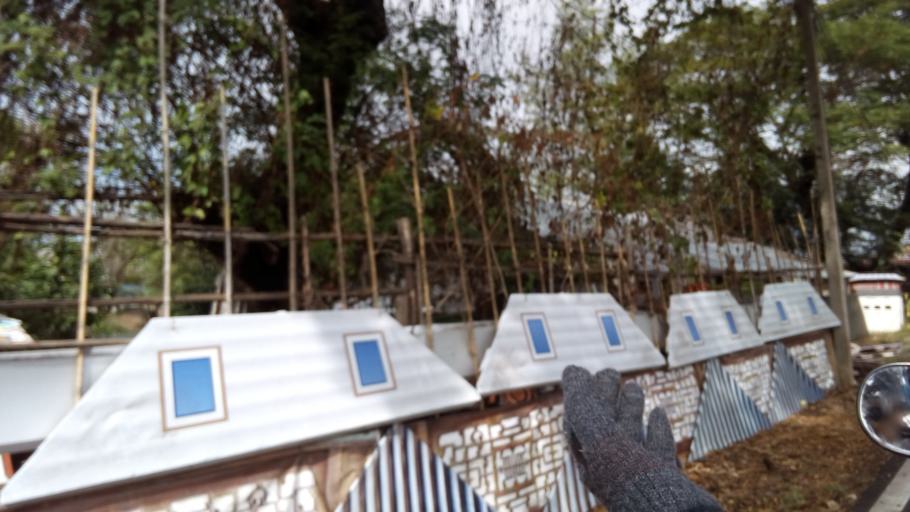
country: TH
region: Pathum Thani
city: Nong Suea
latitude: 14.0673
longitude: 100.8684
